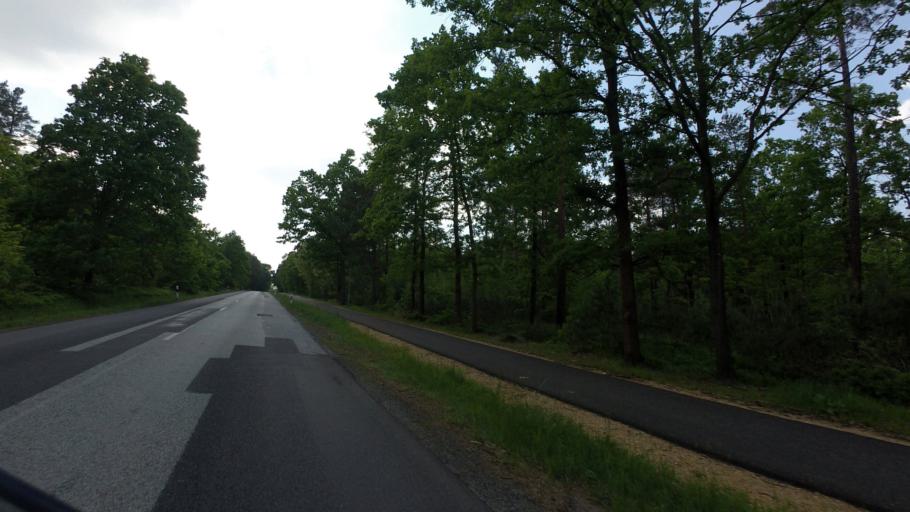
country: DE
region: Saxony
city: Mucka
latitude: 51.3050
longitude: 14.6767
